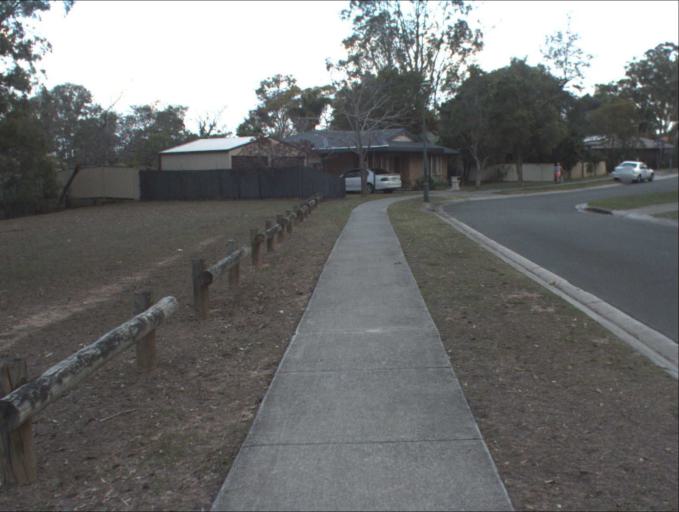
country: AU
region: Queensland
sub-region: Logan
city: Waterford West
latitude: -27.6790
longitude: 153.1344
